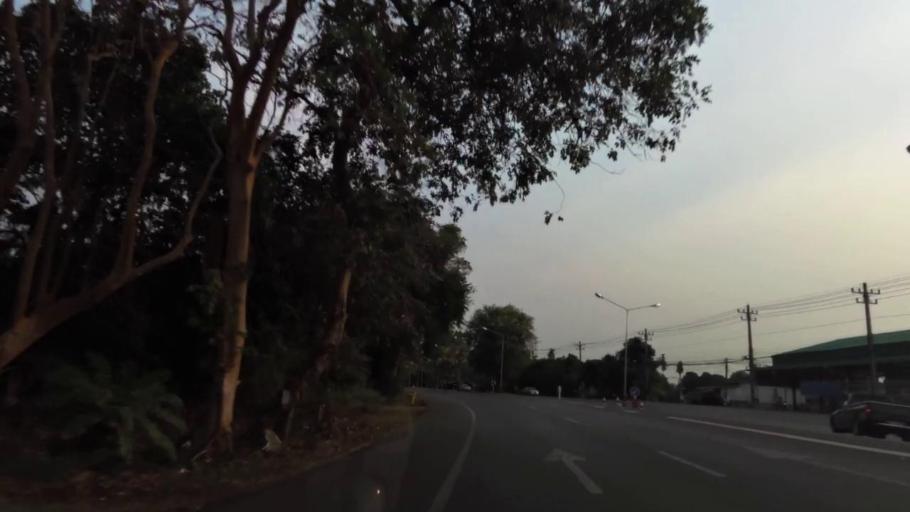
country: TH
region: Chanthaburi
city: Khlung
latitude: 12.4880
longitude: 102.1750
